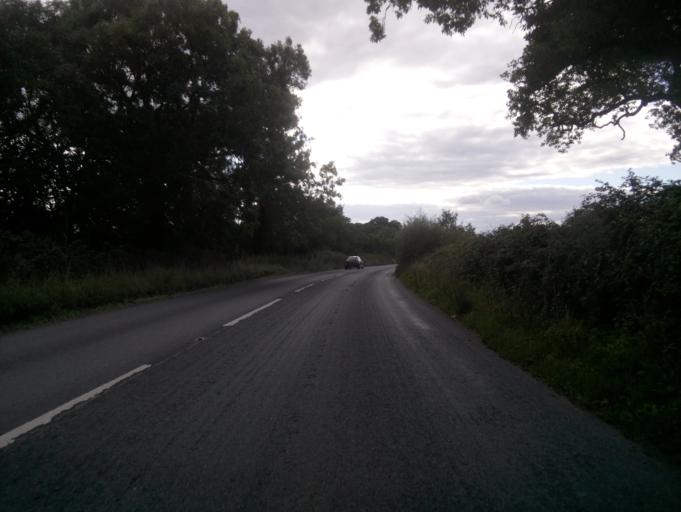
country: GB
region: England
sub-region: Devon
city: Topsham
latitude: 50.7074
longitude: -3.4198
